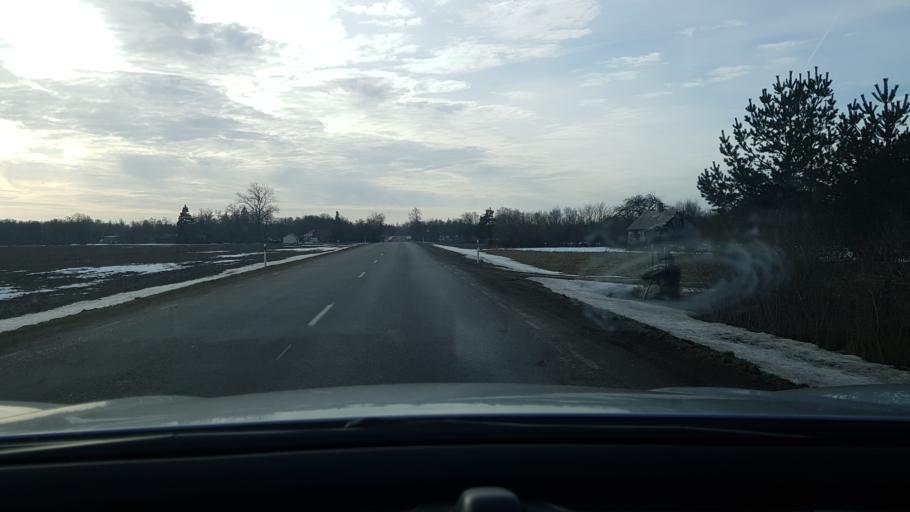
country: EE
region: Saare
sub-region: Kuressaare linn
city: Kuressaare
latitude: 58.3120
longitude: 22.5432
